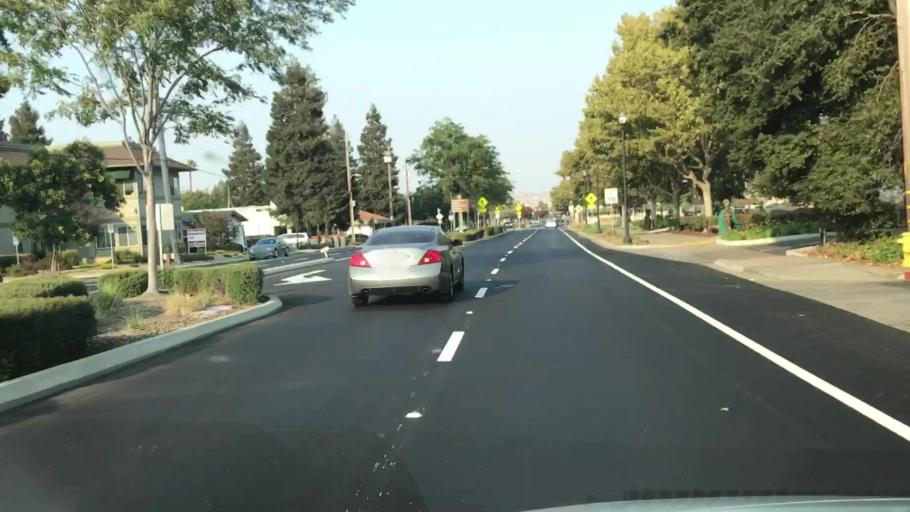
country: US
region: California
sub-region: Alameda County
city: Dublin
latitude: 37.7007
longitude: -121.9402
